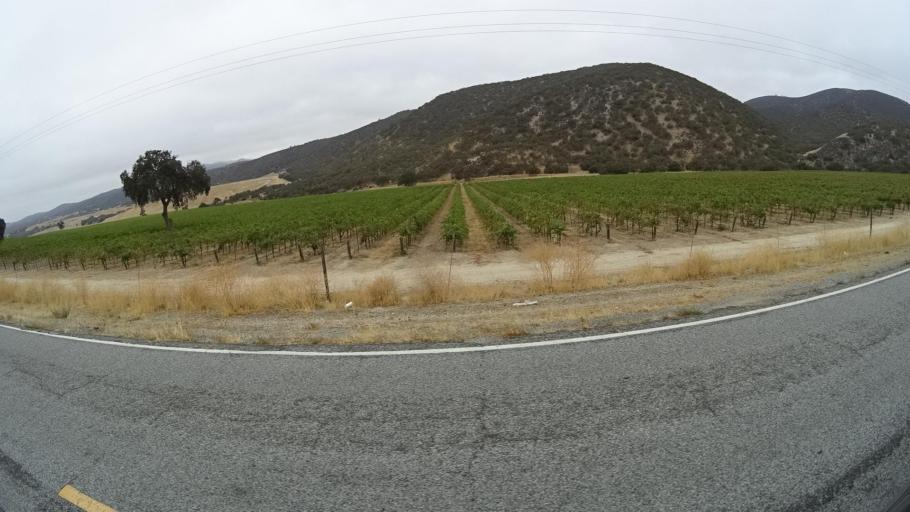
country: US
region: California
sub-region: San Luis Obispo County
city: Lake Nacimiento
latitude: 35.8858
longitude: -120.9148
